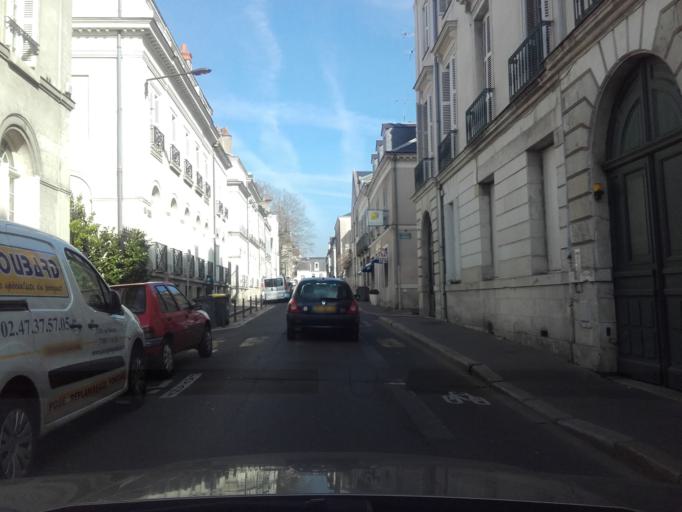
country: FR
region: Centre
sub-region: Departement d'Indre-et-Loire
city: Tours
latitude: 47.3898
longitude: 0.6842
